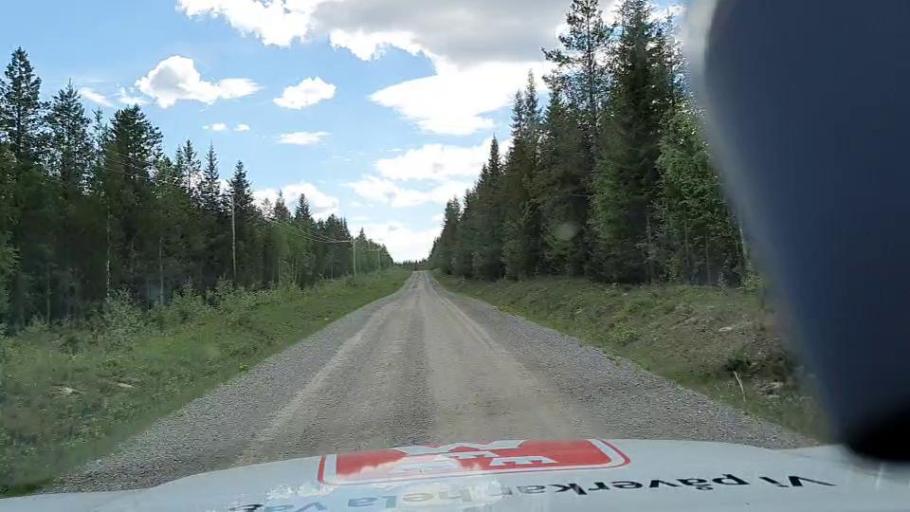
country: SE
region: Jaemtland
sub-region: Stroemsunds Kommun
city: Stroemsund
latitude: 64.5355
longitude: 15.5983
